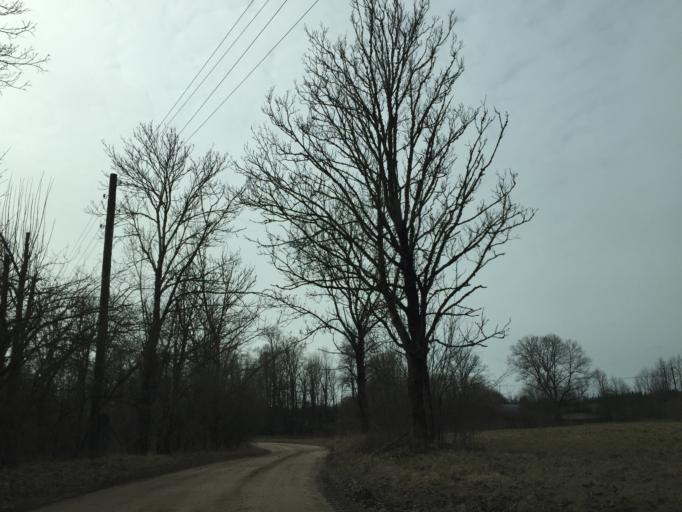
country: LV
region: Jekabpils Rajons
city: Jekabpils
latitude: 56.4772
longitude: 26.0344
